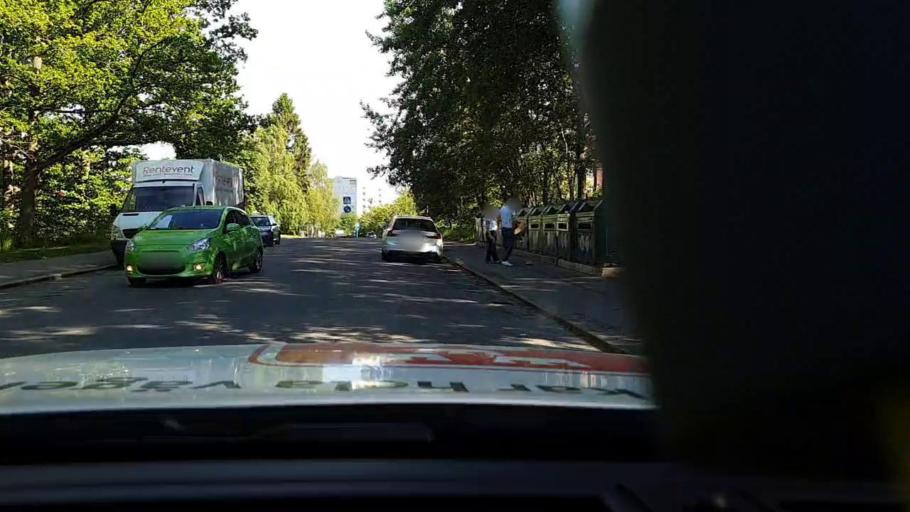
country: SE
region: Stockholm
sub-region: Stockholms Kommun
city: Arsta
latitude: 59.2671
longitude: 18.0315
